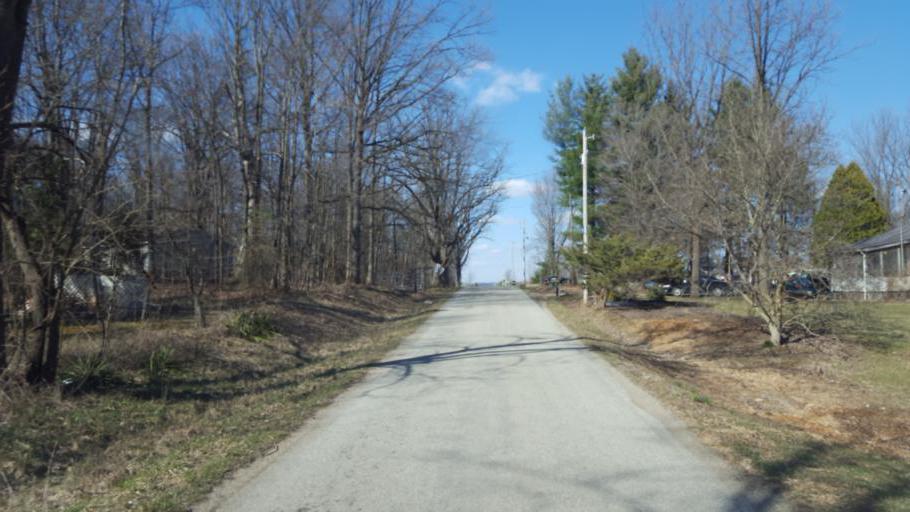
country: US
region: Ohio
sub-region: Knox County
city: Centerburg
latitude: 40.4381
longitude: -82.6785
